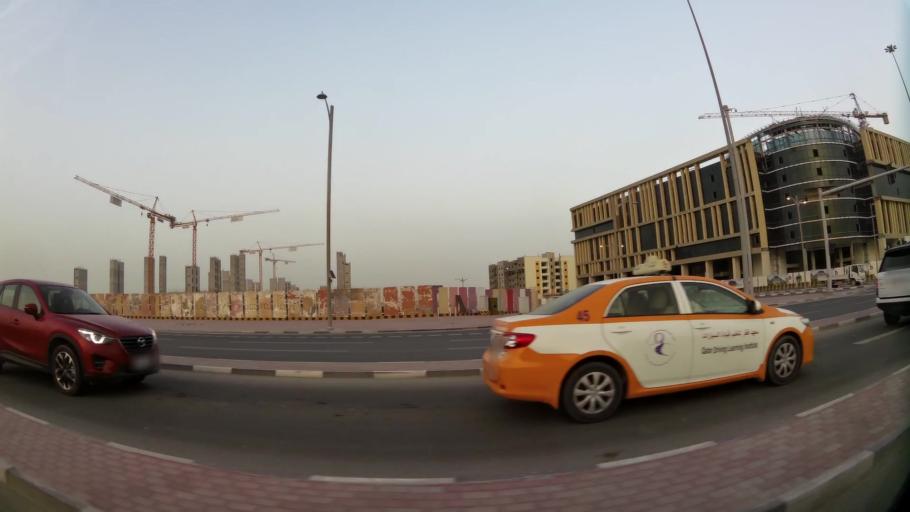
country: QA
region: Baladiyat ad Dawhah
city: Doha
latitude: 25.2535
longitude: 51.4697
